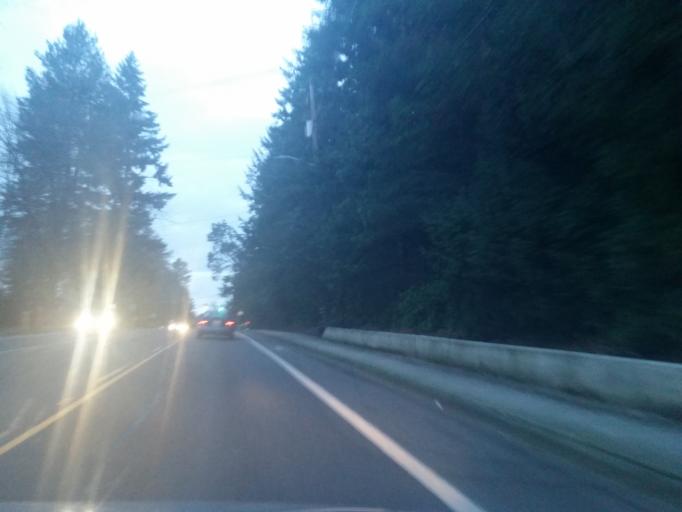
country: US
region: Washington
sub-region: King County
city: Shoreline
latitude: 47.7470
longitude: -122.3130
